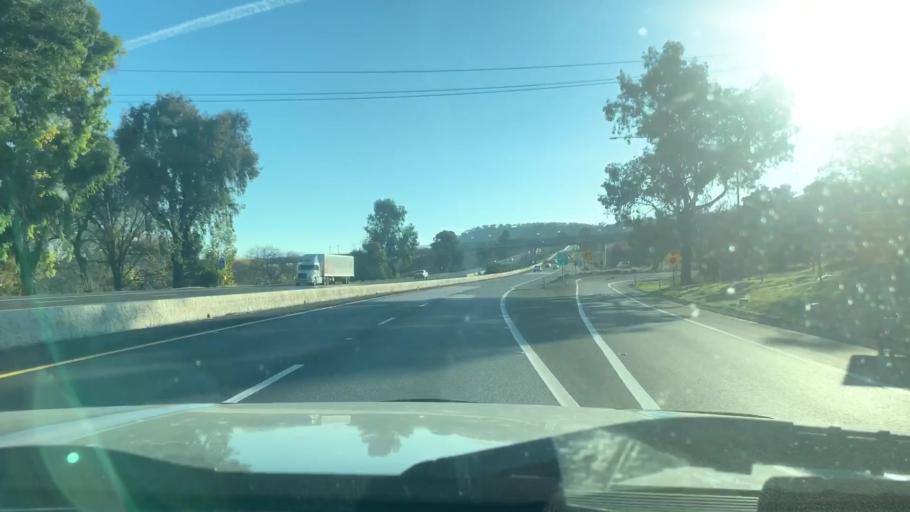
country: US
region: California
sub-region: San Luis Obispo County
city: Paso Robles
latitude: 35.6184
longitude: -120.6867
